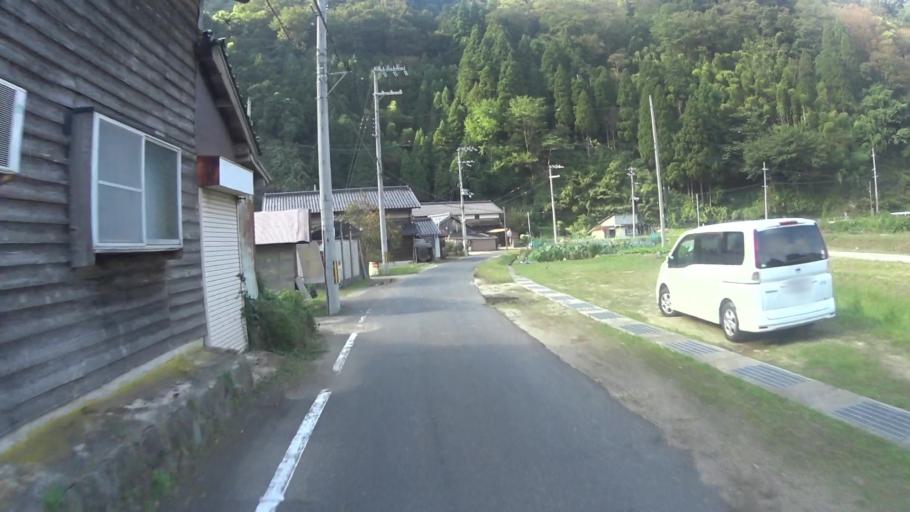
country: JP
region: Kyoto
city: Miyazu
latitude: 35.7357
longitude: 135.1528
